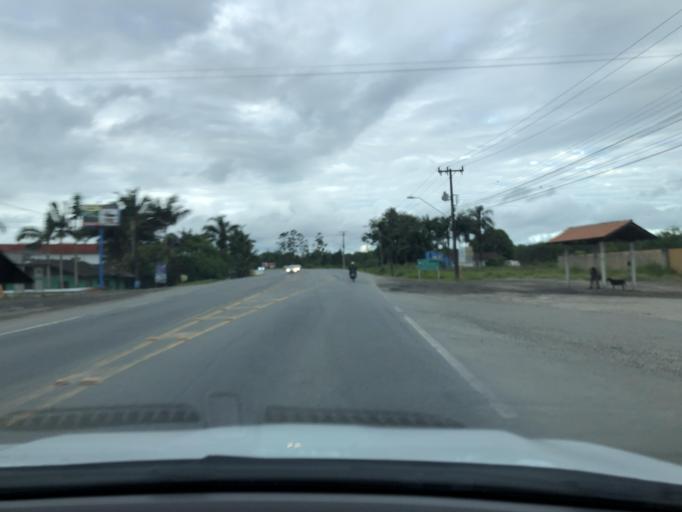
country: BR
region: Santa Catarina
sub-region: Joinville
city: Joinville
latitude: -26.4133
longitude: -48.7584
